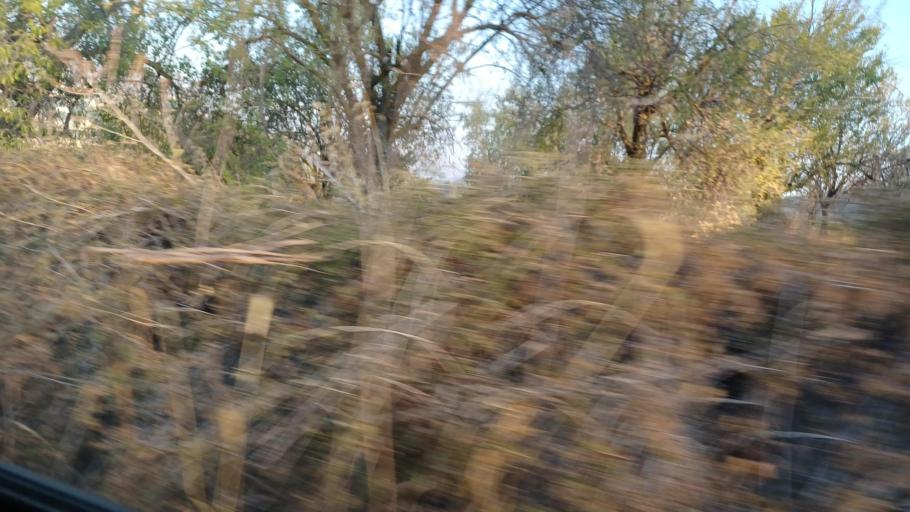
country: CY
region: Pafos
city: Tala
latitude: 34.9172
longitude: 32.4898
